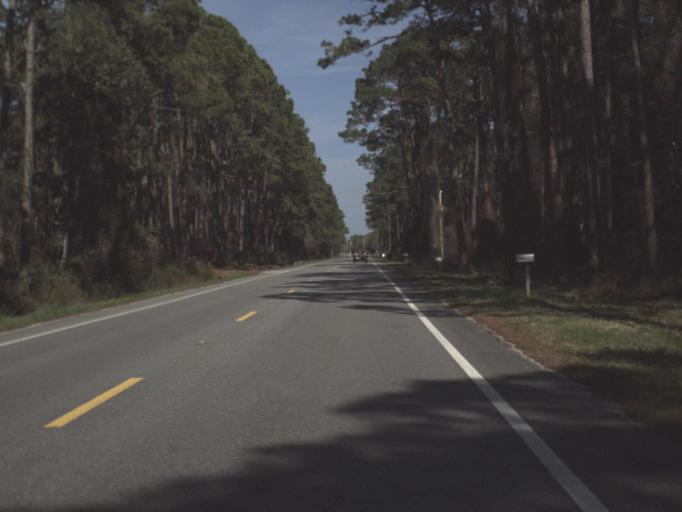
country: US
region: Florida
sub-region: Franklin County
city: Carrabelle
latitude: 29.8081
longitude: -84.7296
